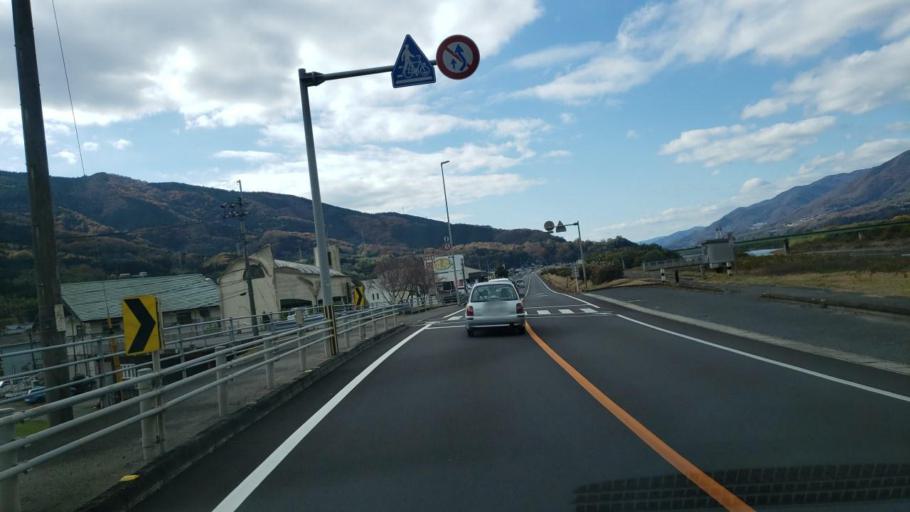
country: JP
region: Tokushima
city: Wakimachi
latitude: 34.0527
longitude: 134.1179
